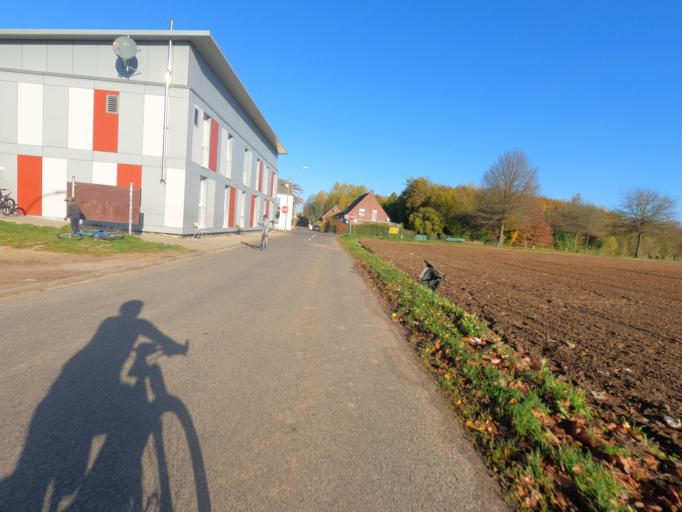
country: DE
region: North Rhine-Westphalia
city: Erkelenz
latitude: 51.0854
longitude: 6.3412
